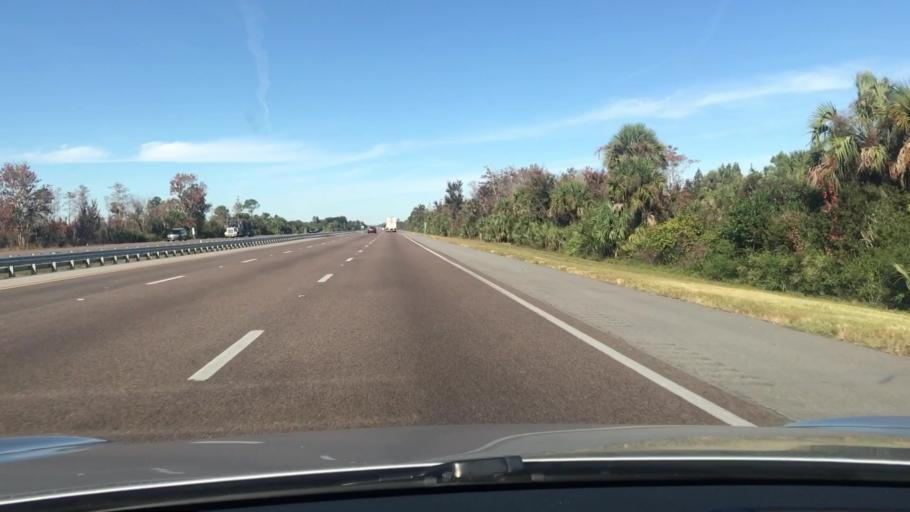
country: US
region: Florida
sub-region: Volusia County
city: Oak Hill
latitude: 28.7971
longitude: -80.9010
